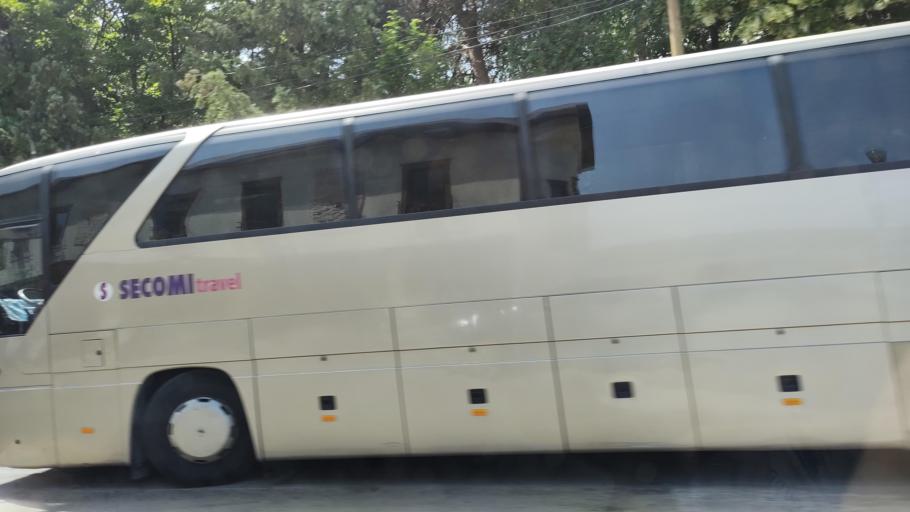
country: RO
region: Mehedinti
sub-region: Municipiul Orsova
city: Orsova
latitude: 44.7293
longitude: 22.4015
